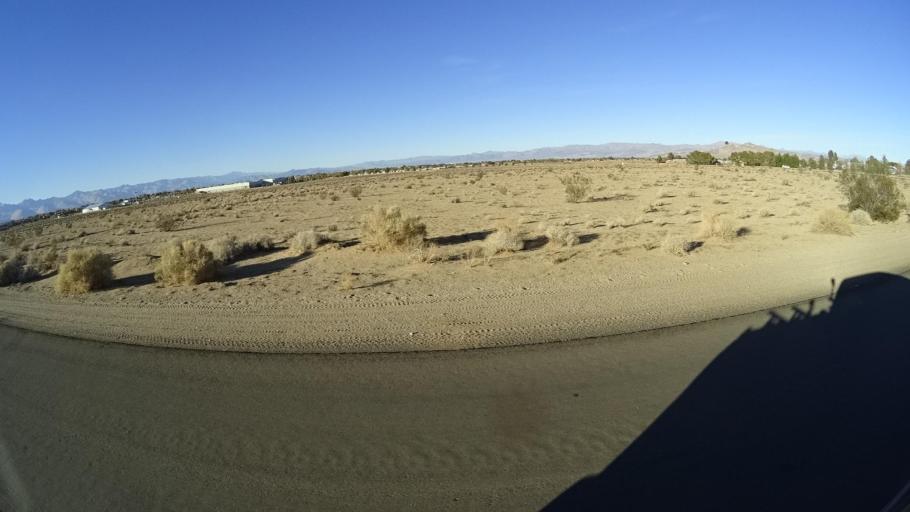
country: US
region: California
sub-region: Kern County
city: Ridgecrest
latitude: 35.6003
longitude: -117.6633
